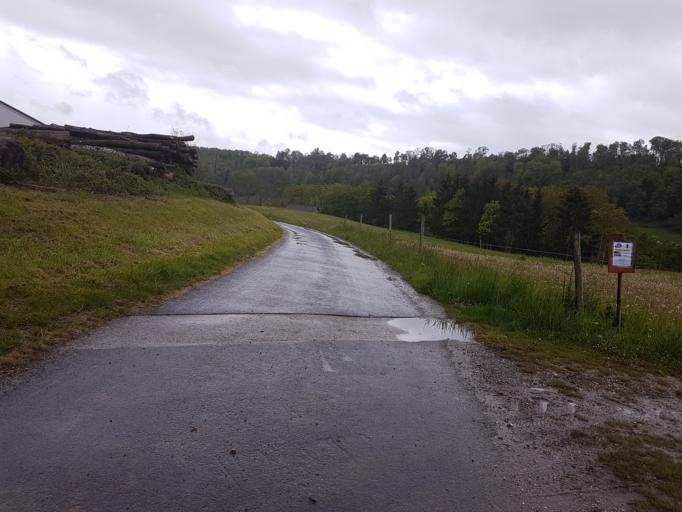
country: CH
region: Vaud
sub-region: Gros-de-Vaud District
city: Penthalaz
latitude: 46.6155
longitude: 6.5194
